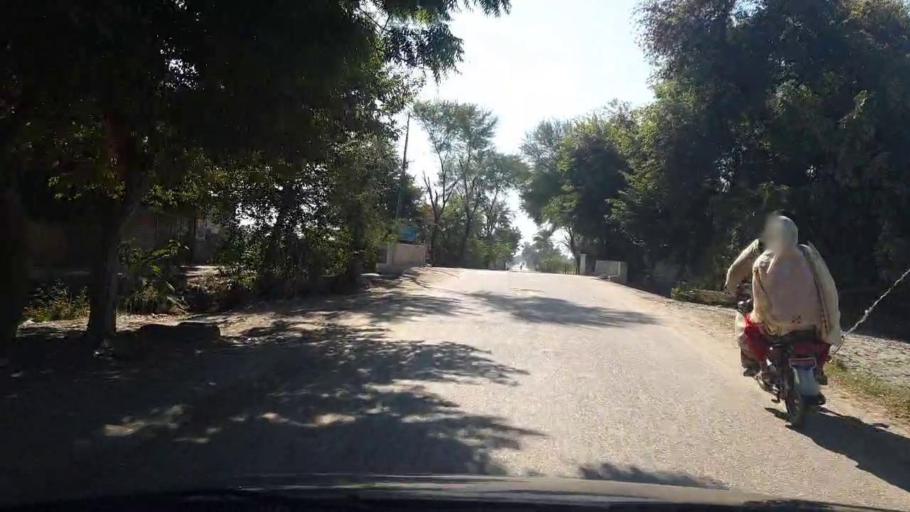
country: PK
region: Sindh
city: Bozdar
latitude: 27.1139
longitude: 68.6345
